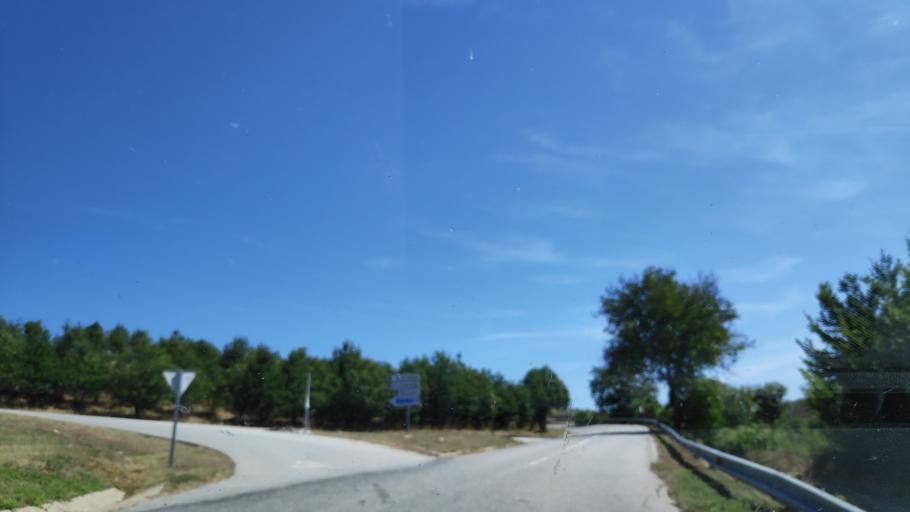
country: PT
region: Braganca
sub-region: Braganca Municipality
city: Braganca
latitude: 41.8548
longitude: -6.7461
